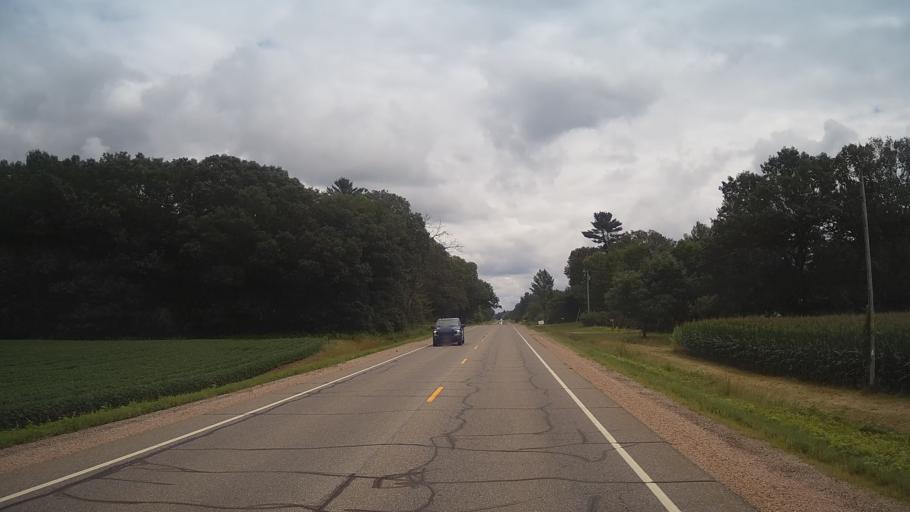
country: US
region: Wisconsin
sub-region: Adams County
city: Friendship
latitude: 44.0396
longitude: -89.9524
